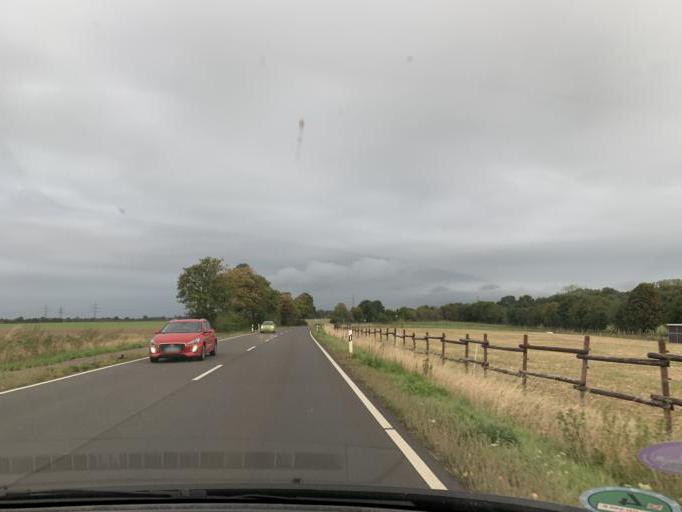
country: DE
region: North Rhine-Westphalia
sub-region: Regierungsbezirk Koln
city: Dueren
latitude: 50.8201
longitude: 6.4420
